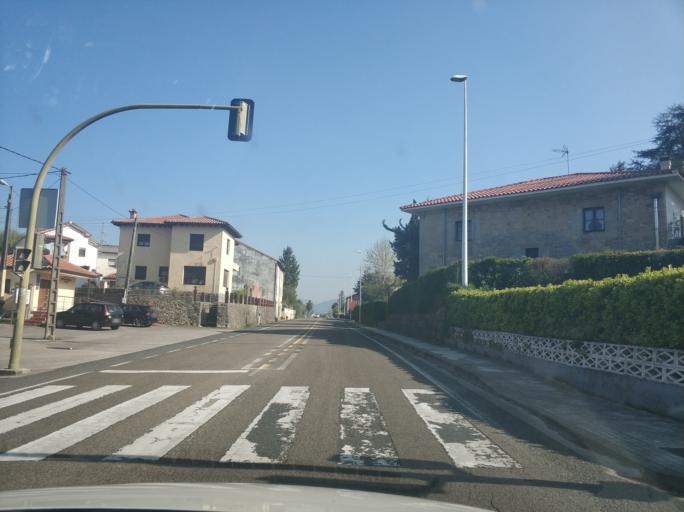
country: ES
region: Cantabria
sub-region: Provincia de Cantabria
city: Barcena de Cicero
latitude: 43.4143
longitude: -3.4898
